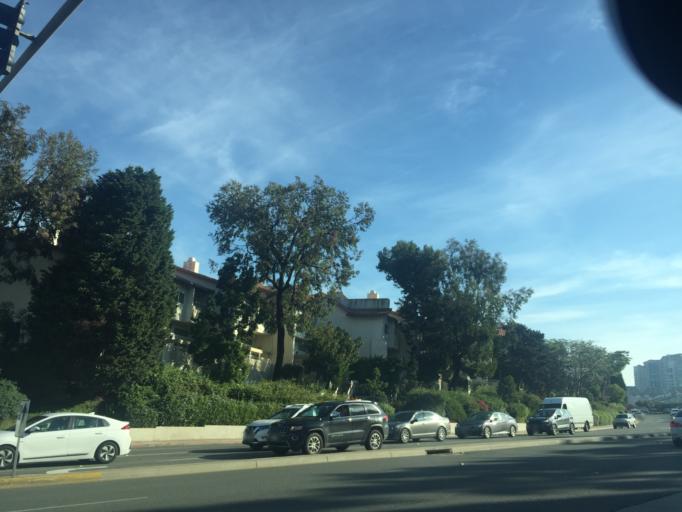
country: US
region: California
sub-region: San Diego County
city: La Jolla
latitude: 32.8707
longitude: -117.2235
